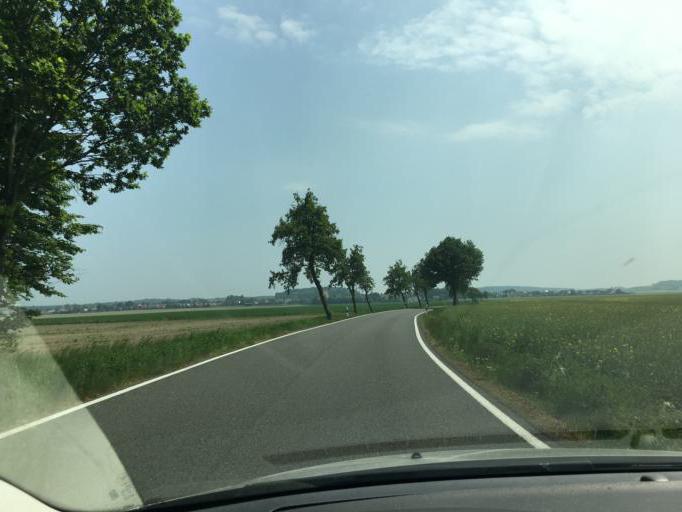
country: DE
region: Saxony
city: Naunhof
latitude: 51.2772
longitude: 12.6198
